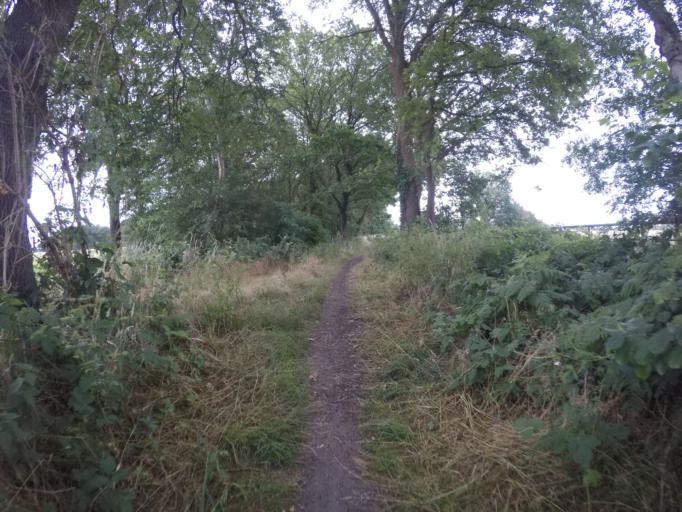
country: DE
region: North Rhine-Westphalia
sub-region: Regierungsbezirk Dusseldorf
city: Bocholt
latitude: 51.8037
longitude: 6.6252
